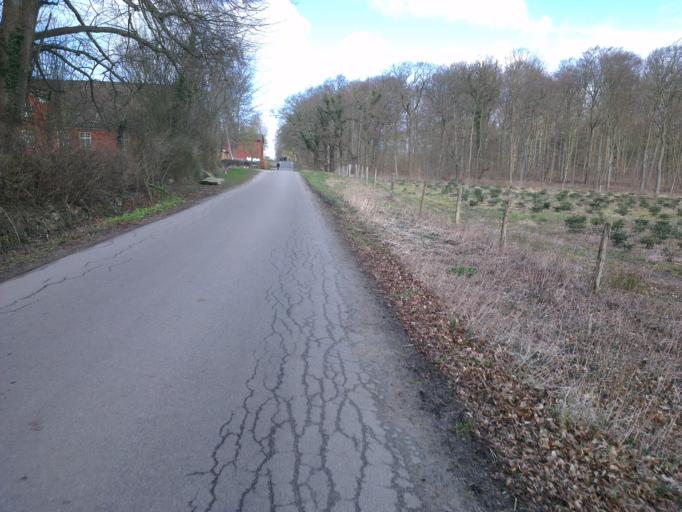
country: DK
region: Capital Region
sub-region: Frederikssund Kommune
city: Jaegerspris
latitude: 55.8699
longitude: 11.9861
